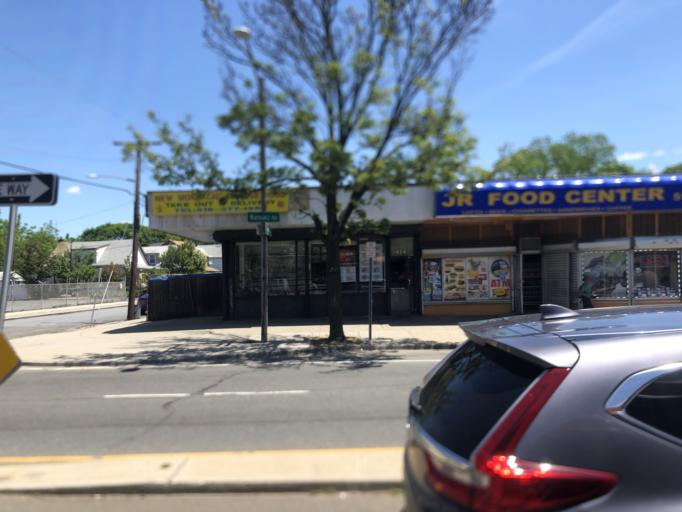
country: US
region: New York
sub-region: Nassau County
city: Roosevelt
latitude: 40.6841
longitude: -73.5925
